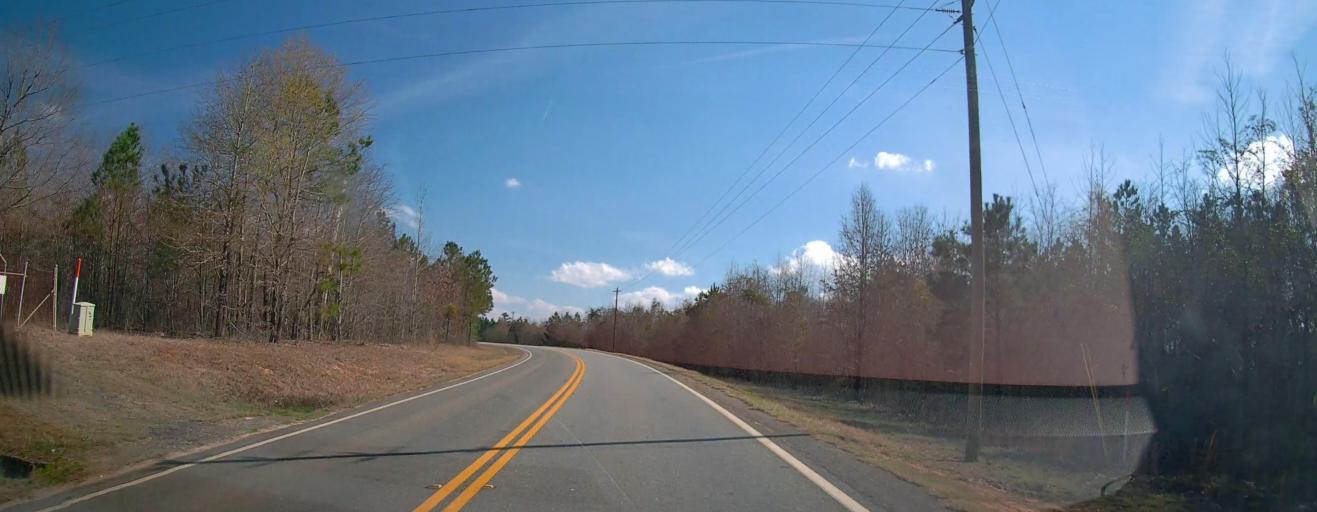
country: US
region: Georgia
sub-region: Wilkinson County
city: Gordon
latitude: 32.8474
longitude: -83.3403
